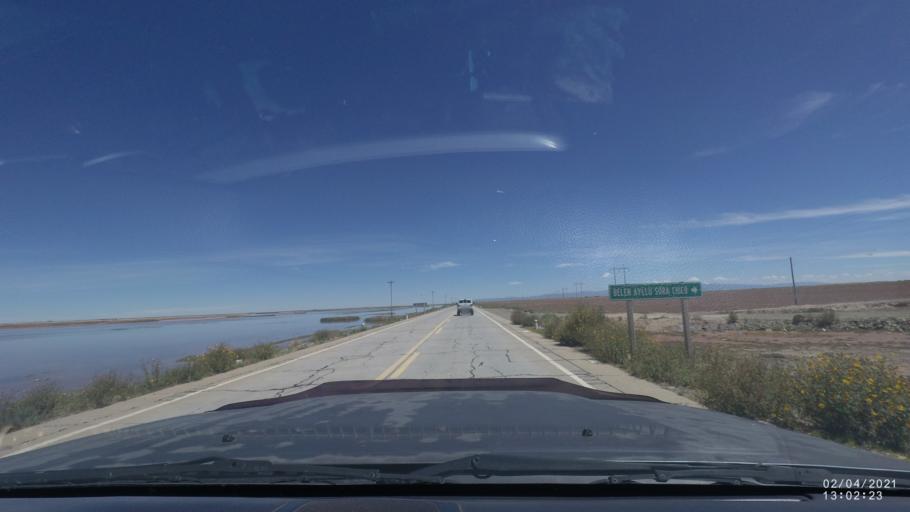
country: BO
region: Oruro
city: Oruro
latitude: -18.0484
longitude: -67.1814
